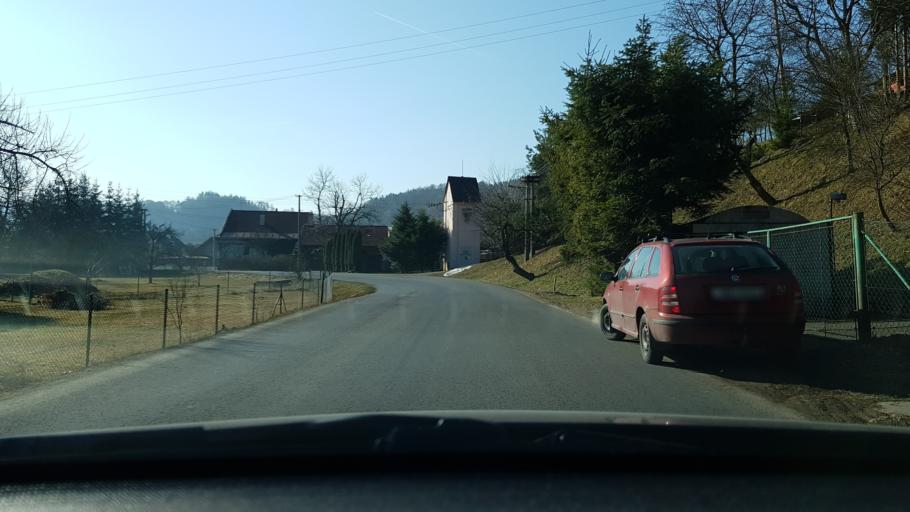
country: CZ
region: Olomoucky
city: Olsany
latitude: 49.9666
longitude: 16.8593
